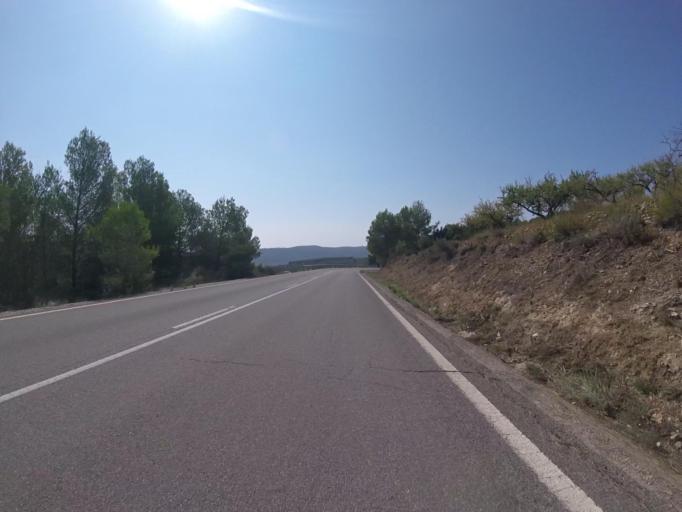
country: ES
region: Valencia
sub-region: Provincia de Castello
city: Adzaneta
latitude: 40.2400
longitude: -0.1882
